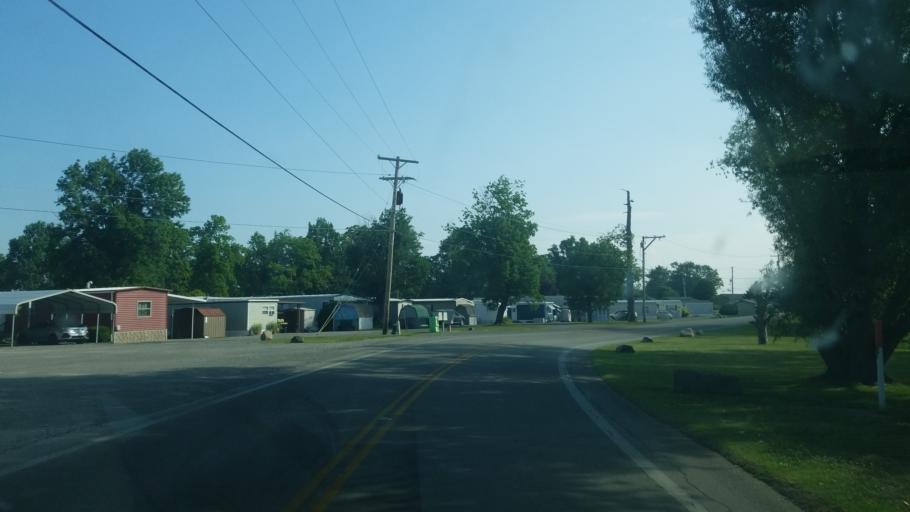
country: US
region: Ohio
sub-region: Logan County
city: Russells Point
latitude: 40.4862
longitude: -83.8624
